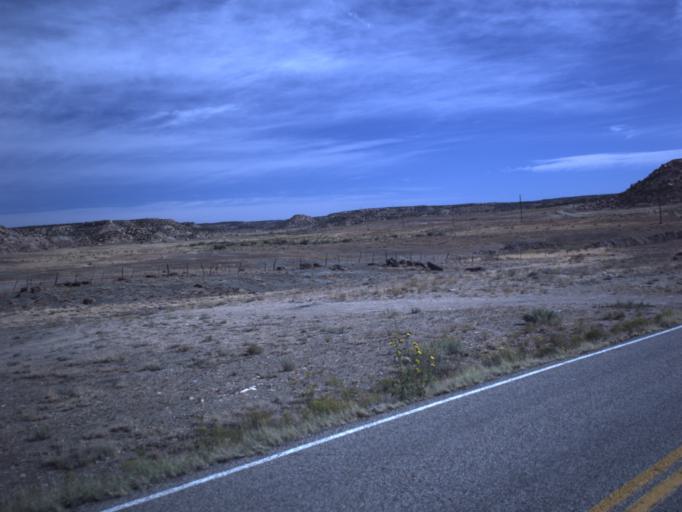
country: US
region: Utah
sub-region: San Juan County
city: Blanding
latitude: 37.4195
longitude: -109.4243
